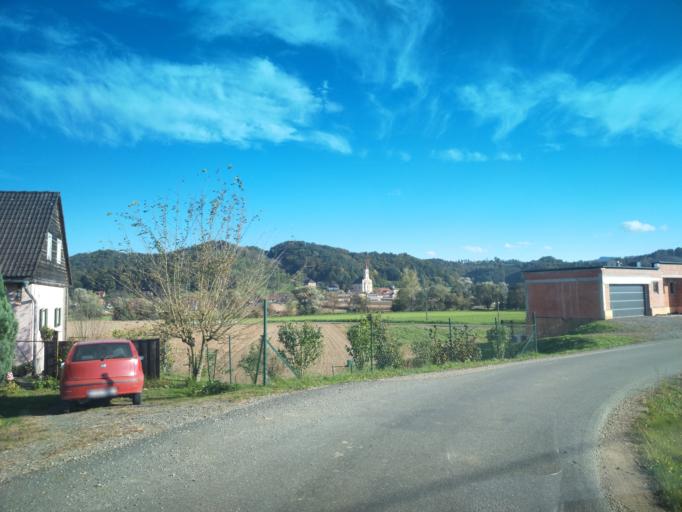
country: AT
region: Styria
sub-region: Politischer Bezirk Leibnitz
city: Sankt Johann im Saggautal
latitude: 46.7076
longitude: 15.3922
